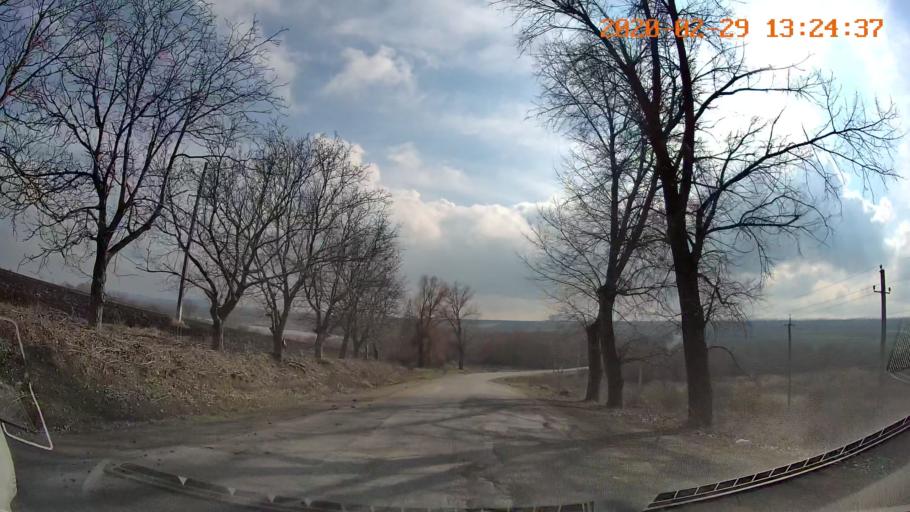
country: MD
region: Telenesti
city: Camenca
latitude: 47.9370
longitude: 28.6284
